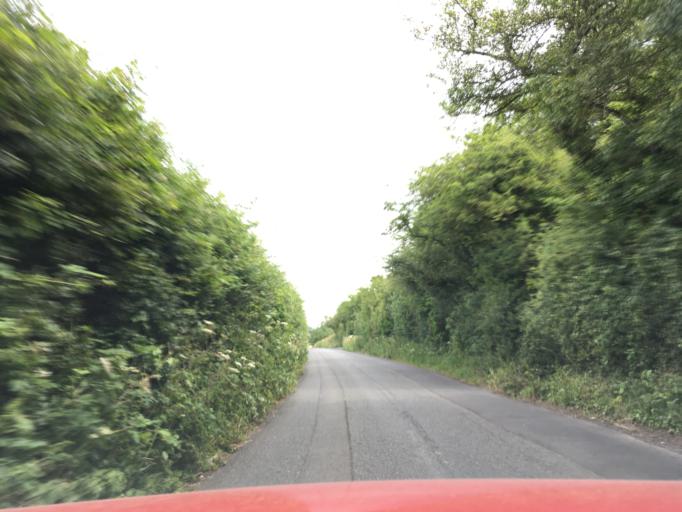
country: GB
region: England
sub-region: Oxfordshire
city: Shipton under Wychwood
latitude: 51.8734
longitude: -1.6677
